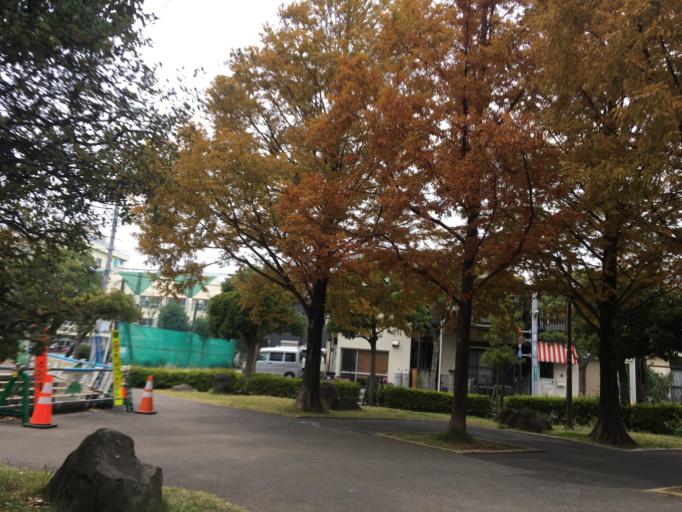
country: JP
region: Tokyo
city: Urayasu
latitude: 35.6505
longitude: 139.8814
